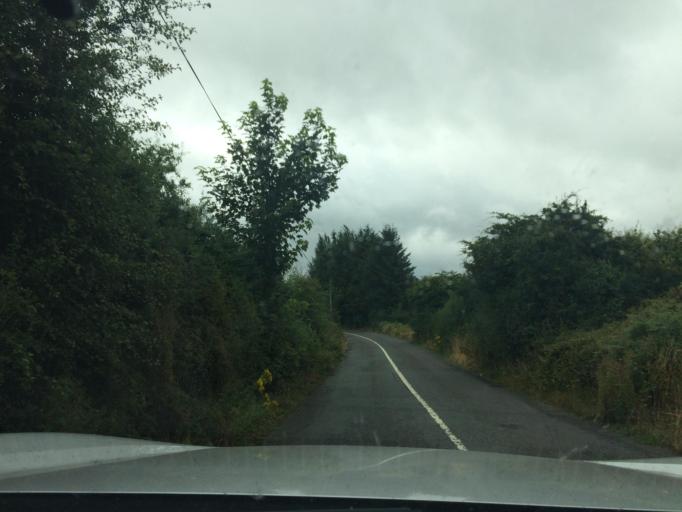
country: IE
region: Munster
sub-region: South Tipperary
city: Cluain Meala
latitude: 52.2266
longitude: -7.7226
